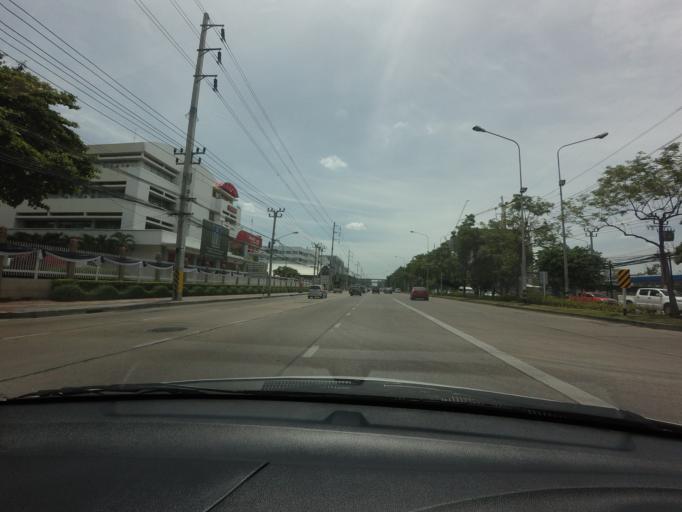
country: TH
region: Bangkok
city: Lak Si
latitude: 13.8891
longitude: 100.5716
